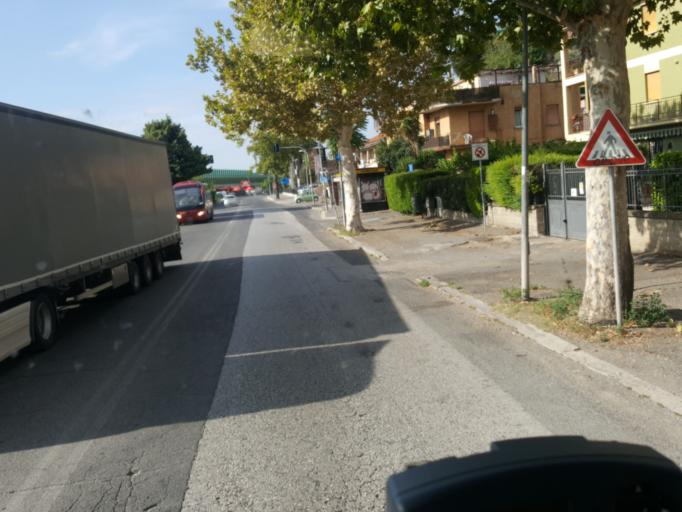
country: IT
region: Latium
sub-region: Citta metropolitana di Roma Capitale
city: Girardi-Bellavista-Terrazze
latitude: 42.1019
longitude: 12.5824
